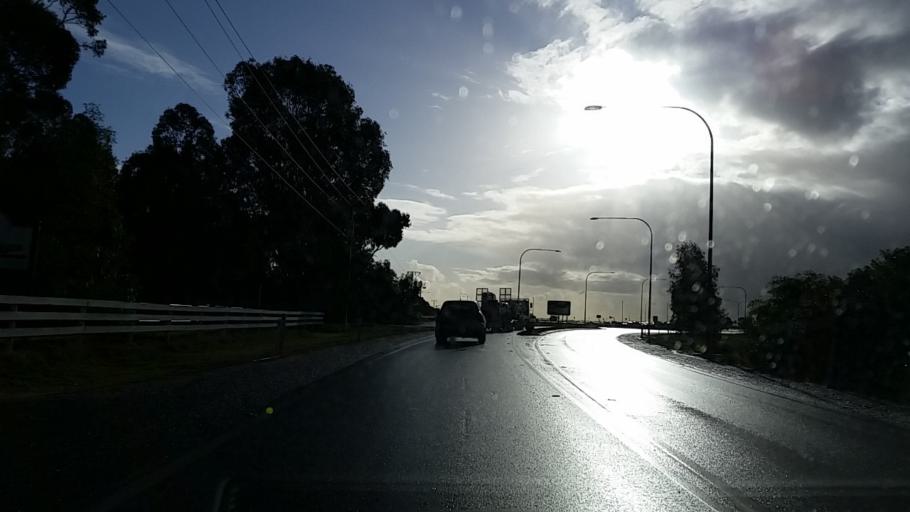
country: AU
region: South Australia
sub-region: Playford
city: Angle Vale
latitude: -34.6838
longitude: 138.6245
